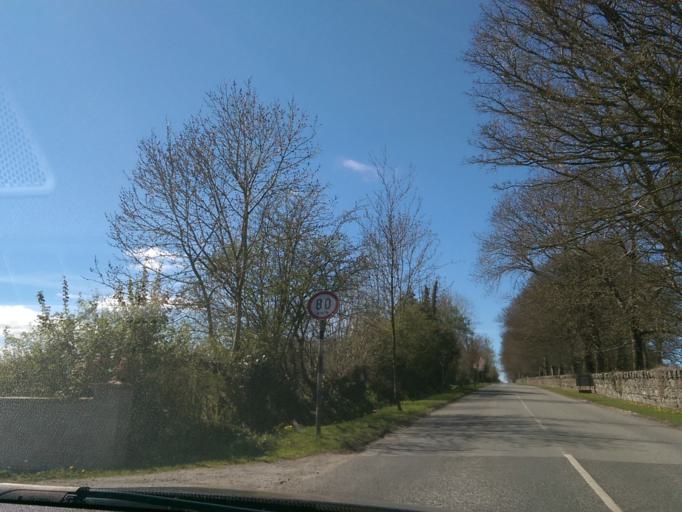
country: IE
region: Leinster
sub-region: Wicklow
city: Baltinglass
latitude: 52.9058
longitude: -6.6090
